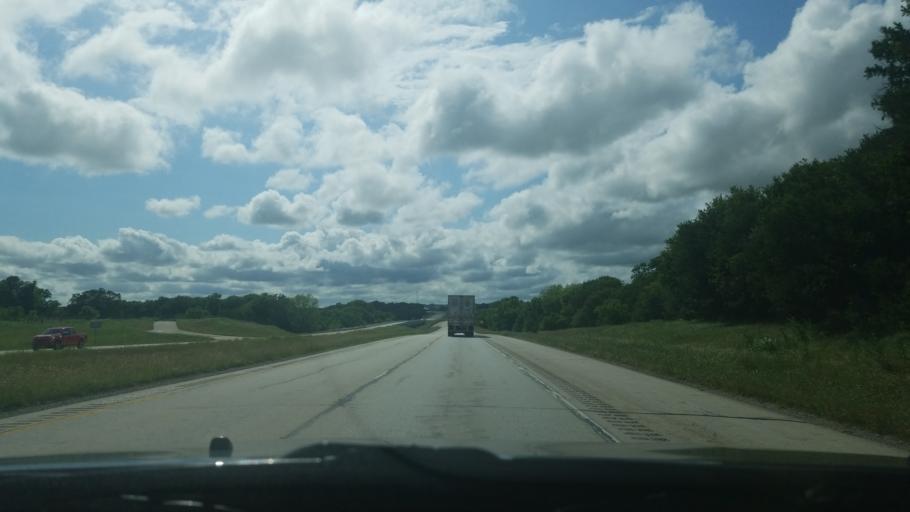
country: US
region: Texas
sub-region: Denton County
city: Ponder
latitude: 33.2483
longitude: -97.3997
